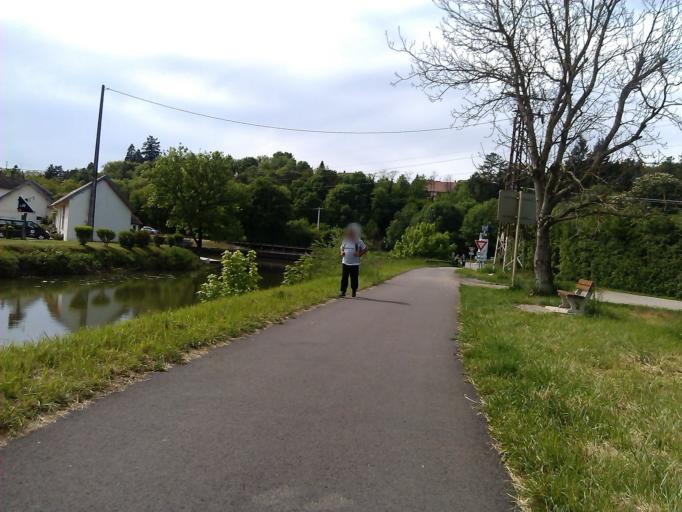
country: FR
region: Franche-Comte
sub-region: Departement du Doubs
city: Saint-Vit
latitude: 47.1744
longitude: 5.7945
